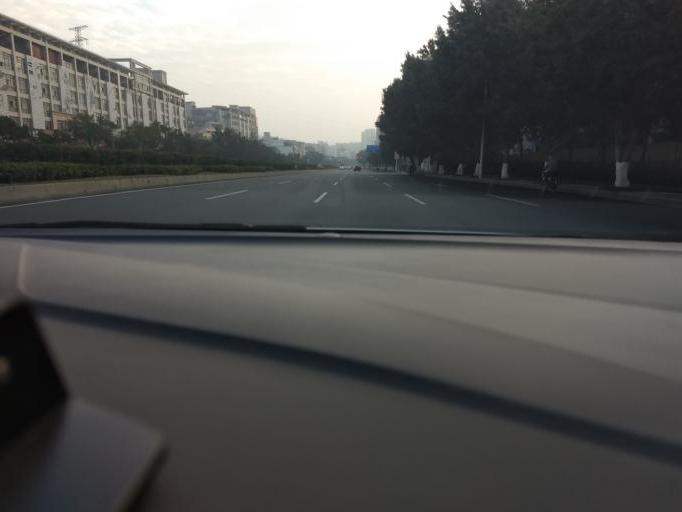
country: CN
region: Guangdong
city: Nansha
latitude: 22.8032
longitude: 113.5379
